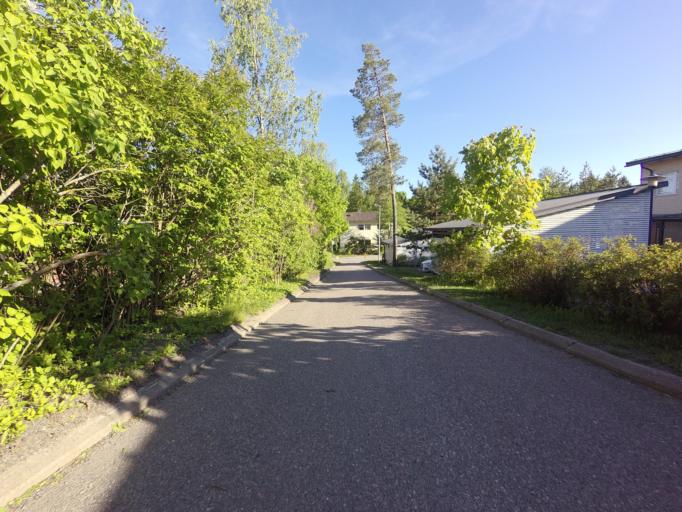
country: FI
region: Uusimaa
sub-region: Helsinki
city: Koukkuniemi
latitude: 60.1719
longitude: 24.7416
